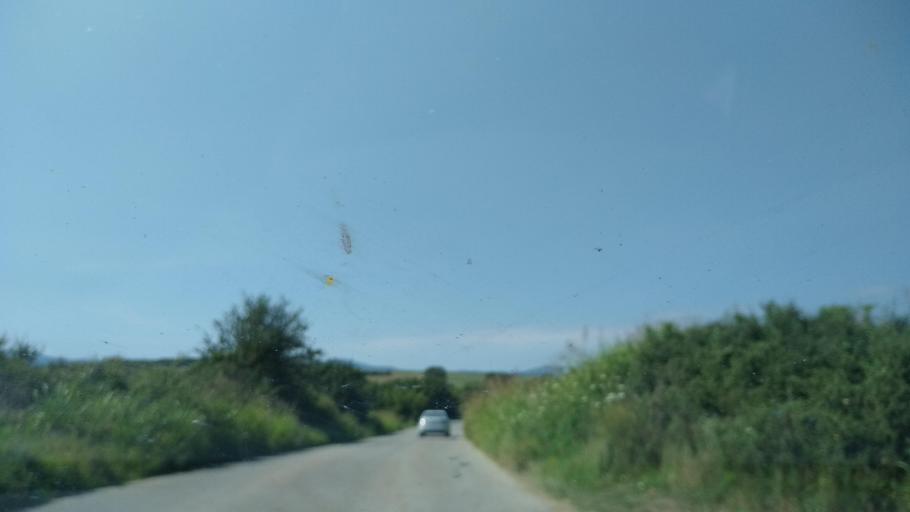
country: GR
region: Central Macedonia
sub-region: Nomos Thessalonikis
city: Nea Apollonia
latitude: 40.6186
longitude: 23.4638
